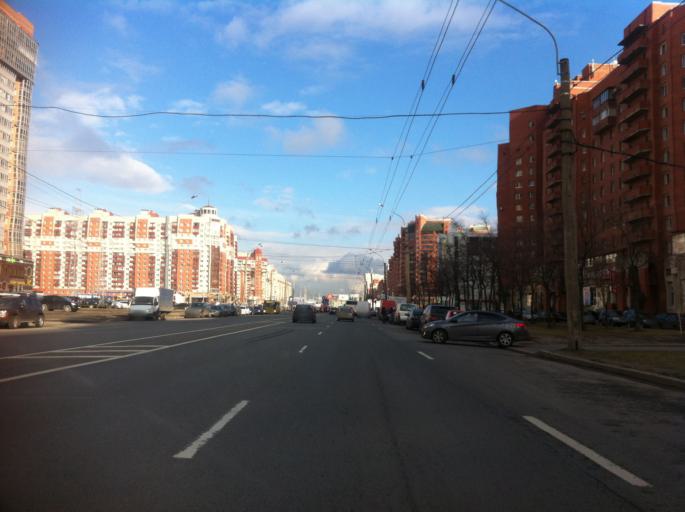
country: RU
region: St.-Petersburg
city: Uritsk
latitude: 59.8574
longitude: 30.1968
